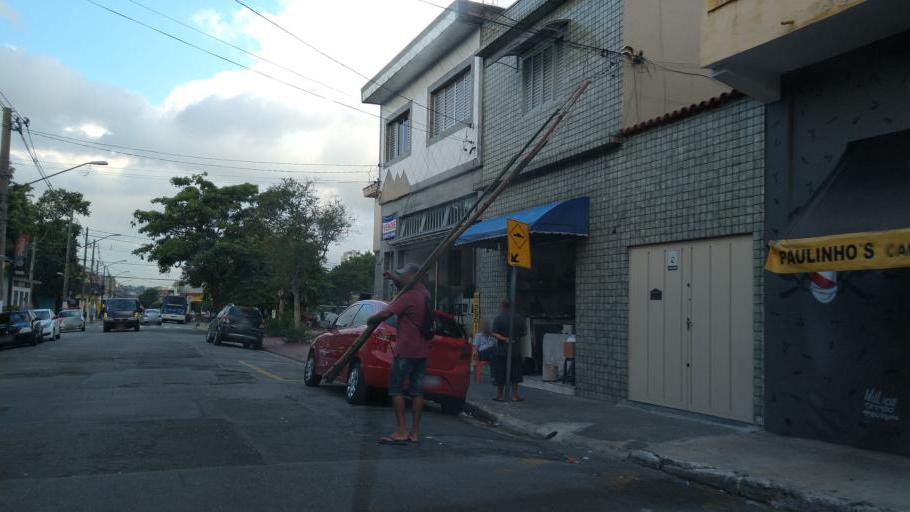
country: BR
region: Sao Paulo
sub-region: Guarulhos
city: Guarulhos
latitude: -23.4845
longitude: -46.5740
